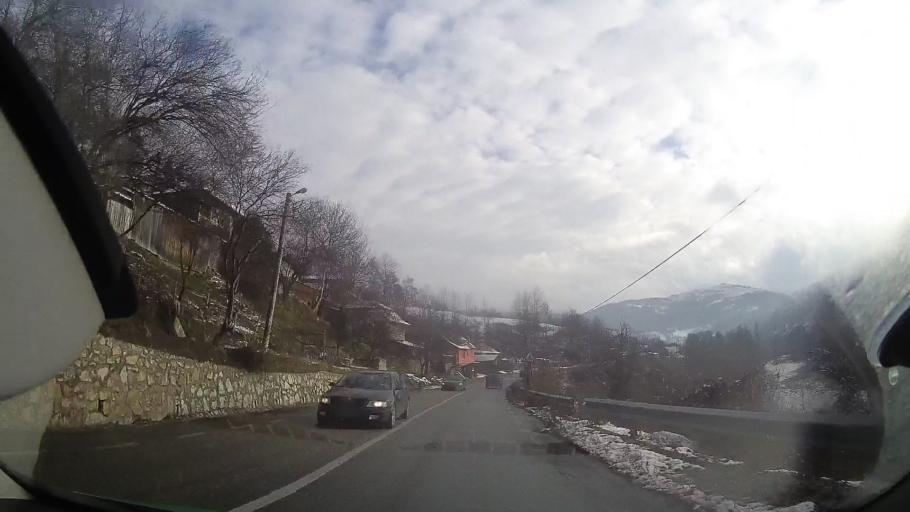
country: RO
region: Alba
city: Salciua de Sus
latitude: 46.3950
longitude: 23.3869
